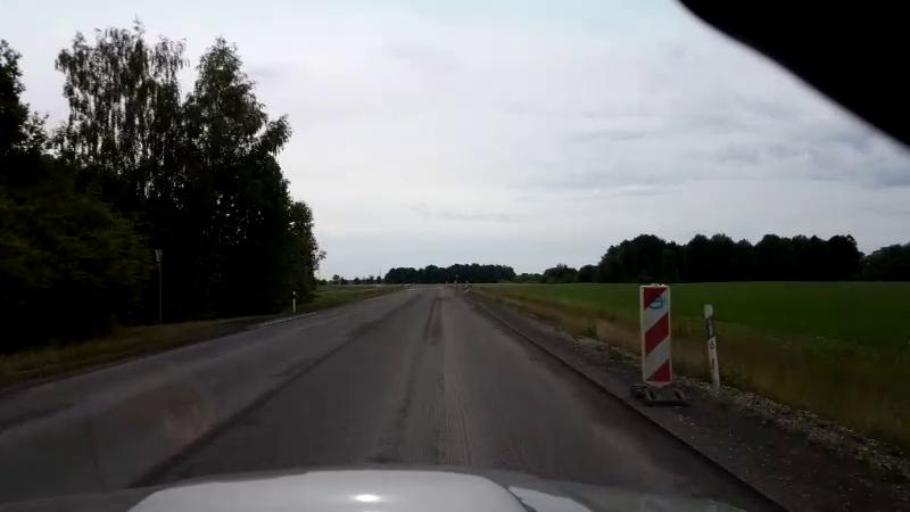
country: LV
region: Bauskas Rajons
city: Bauska
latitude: 56.2963
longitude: 24.3462
